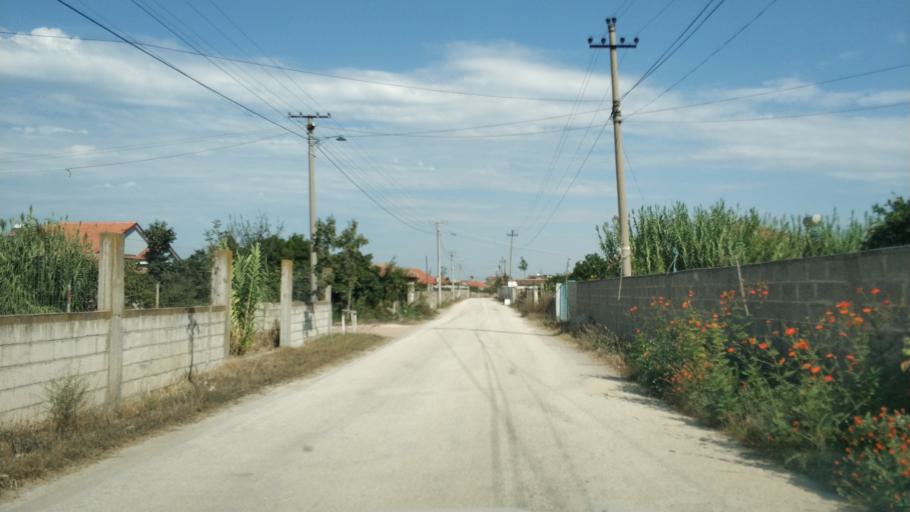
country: AL
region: Fier
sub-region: Rrethi i Lushnjes
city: Divjake
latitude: 40.9906
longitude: 19.5259
